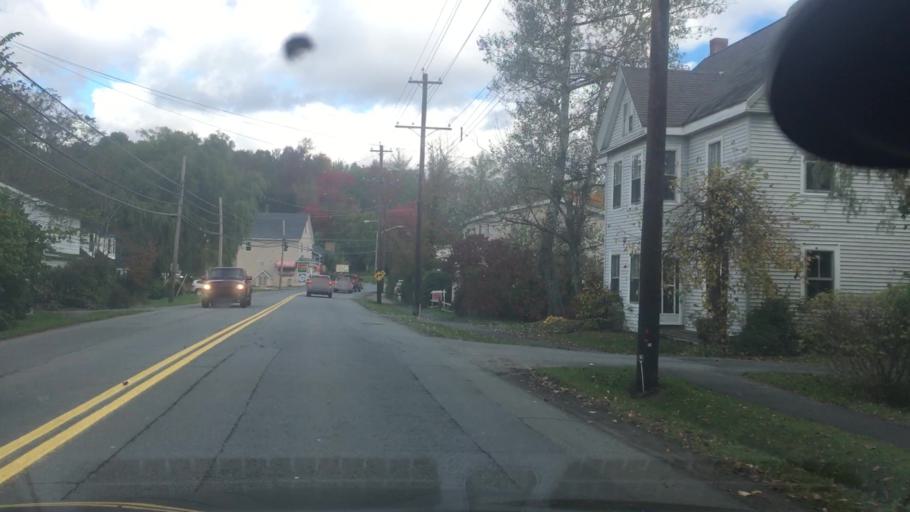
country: CA
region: Nova Scotia
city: Windsor
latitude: 44.9846
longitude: -64.1310
